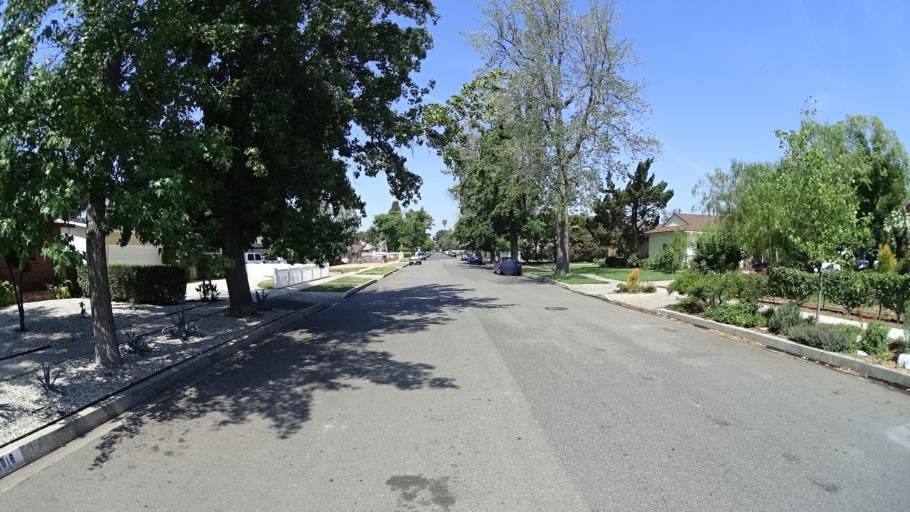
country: US
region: California
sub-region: Los Angeles County
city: Van Nuys
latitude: 34.2039
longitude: -118.4606
